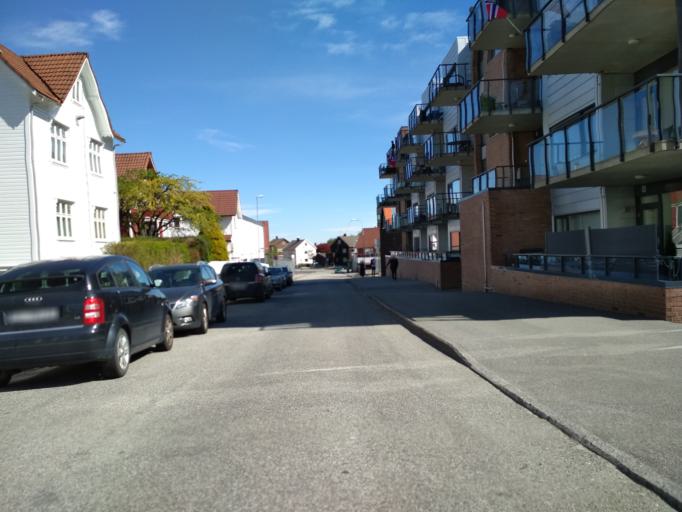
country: NO
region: Rogaland
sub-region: Stavanger
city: Stavanger
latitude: 58.9763
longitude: 5.7152
